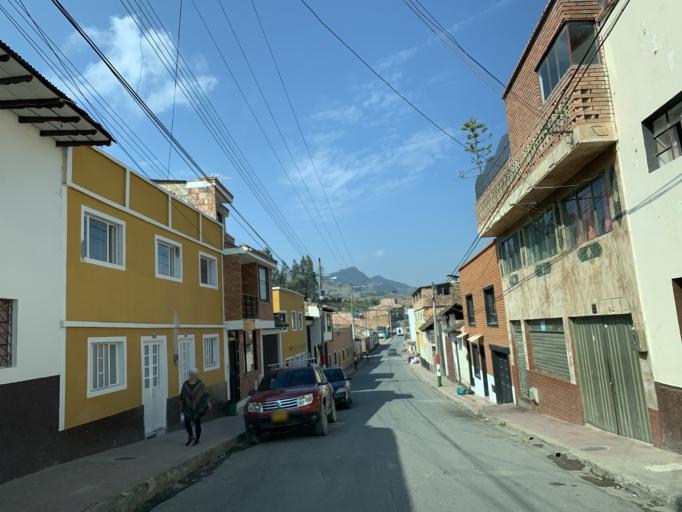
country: CO
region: Boyaca
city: Turmeque
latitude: 5.3223
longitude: -73.4912
